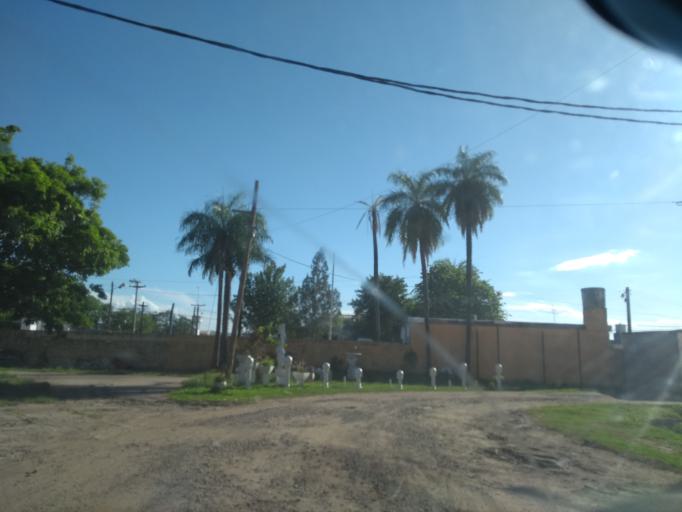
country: AR
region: Chaco
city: Resistencia
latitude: -27.4754
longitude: -58.9616
